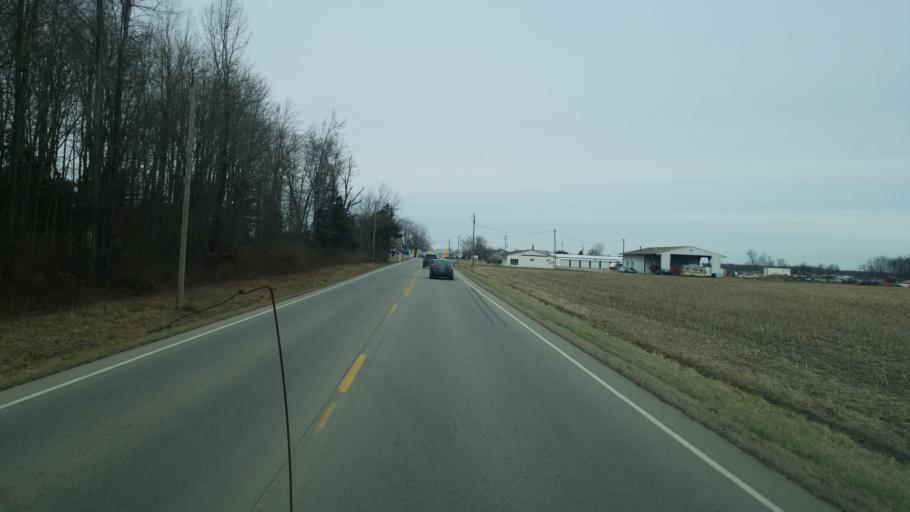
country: US
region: Ohio
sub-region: Adams County
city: Winchester
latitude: 39.0601
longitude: -83.7036
